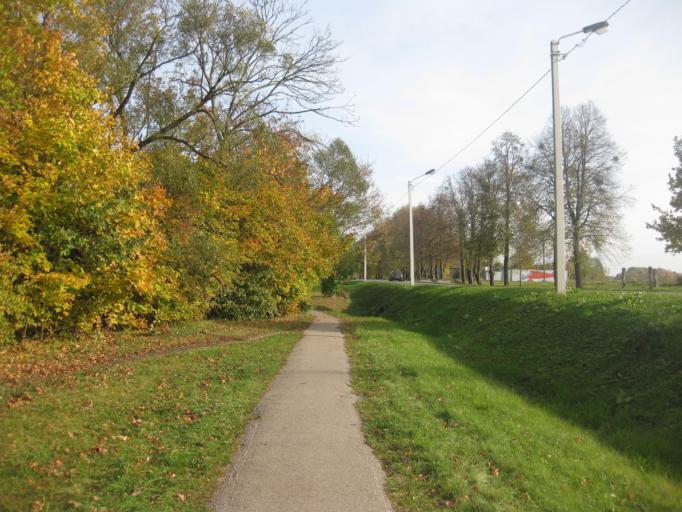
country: LT
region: Kauno apskritis
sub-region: Kaunas
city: Aleksotas
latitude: 54.8897
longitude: 23.8817
